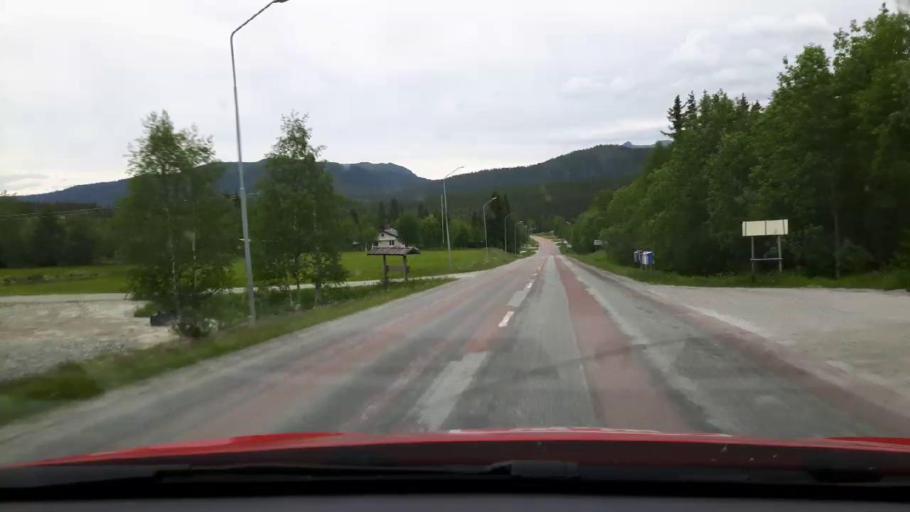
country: NO
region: Hedmark
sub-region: Engerdal
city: Engerdal
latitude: 62.5491
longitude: 12.5611
